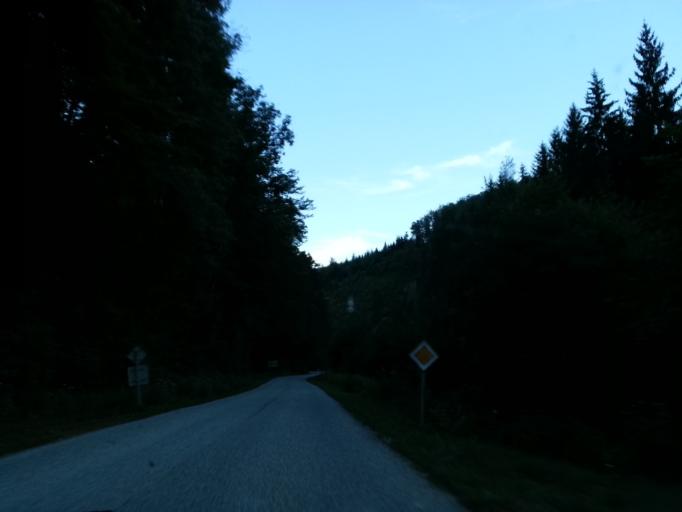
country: DE
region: Rheinland-Pfalz
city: Hirschthal
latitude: 49.0257
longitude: 7.7707
